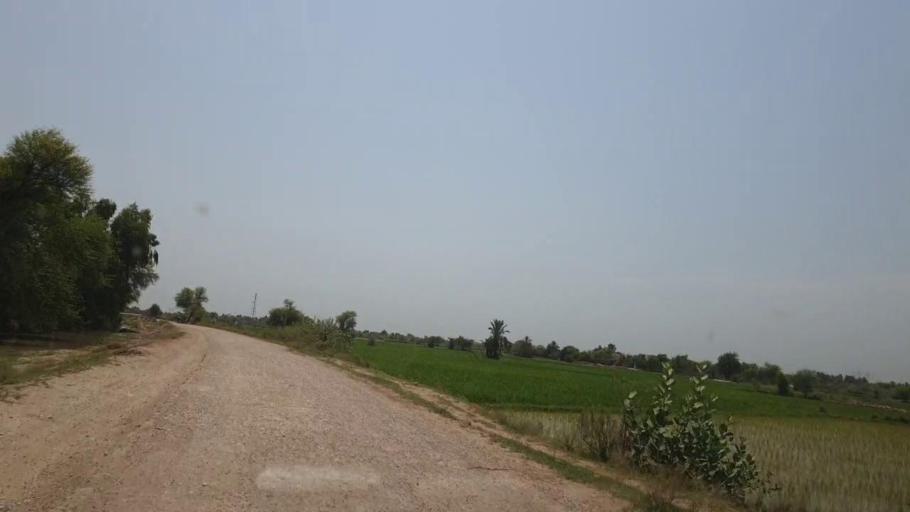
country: PK
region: Sindh
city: Lakhi
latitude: 27.8684
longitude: 68.6078
